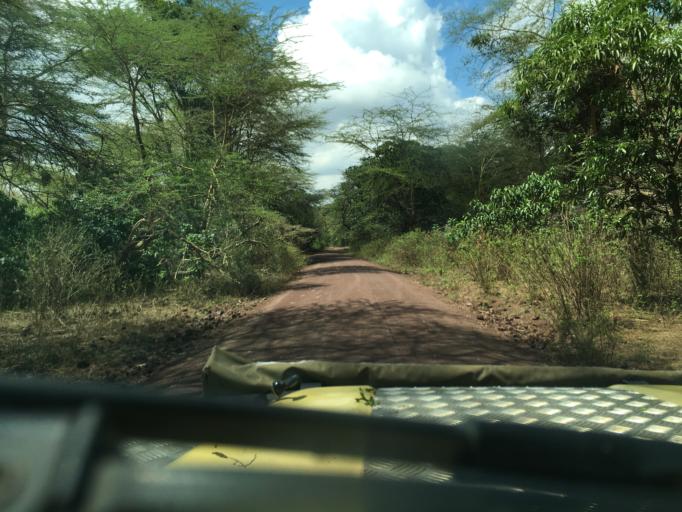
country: TZ
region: Arusha
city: Mto wa Mbu
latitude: -3.4077
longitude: 35.8233
